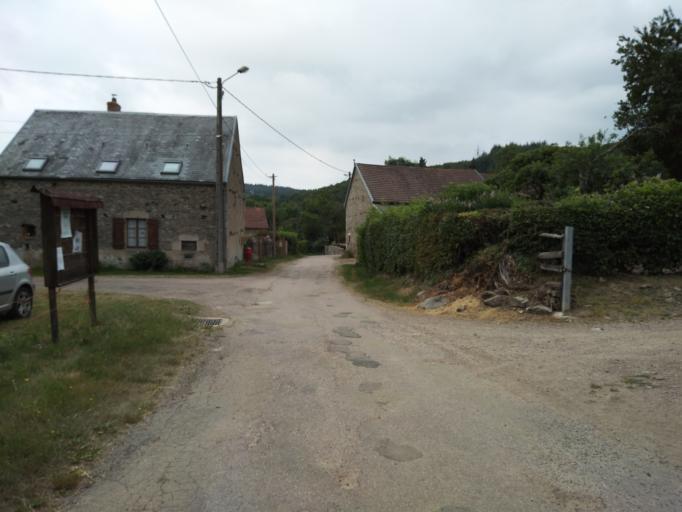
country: FR
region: Bourgogne
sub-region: Departement de la Cote-d'Or
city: Saulieu
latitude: 47.2832
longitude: 4.1220
